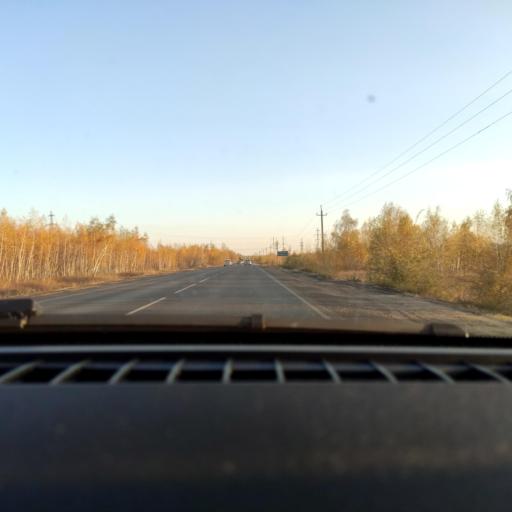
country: RU
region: Voronezj
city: Maslovka
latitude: 51.5861
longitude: 39.2556
